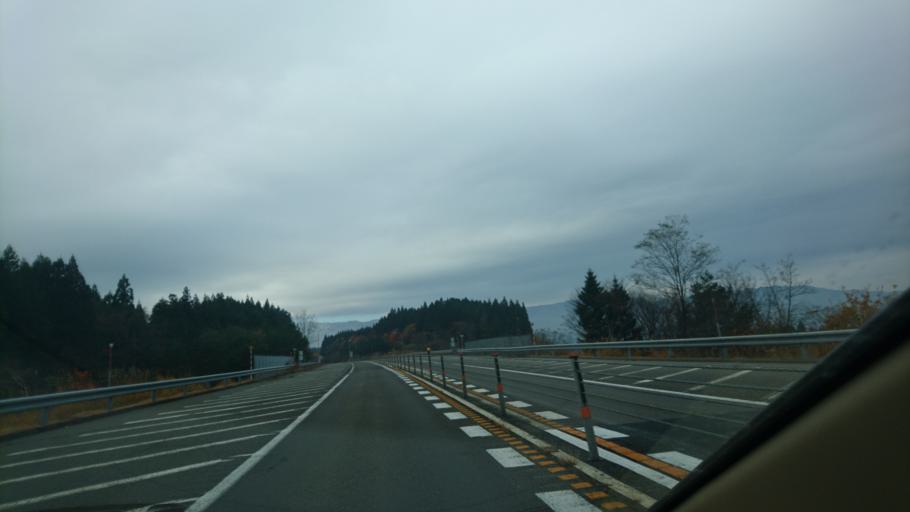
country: JP
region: Iwate
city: Kitakami
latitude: 39.2915
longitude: 140.9852
